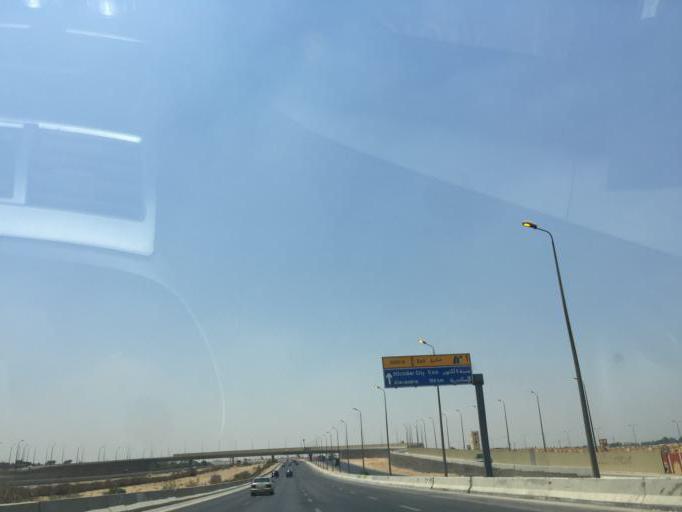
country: EG
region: Al Jizah
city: Awsim
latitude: 30.0786
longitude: 30.9999
